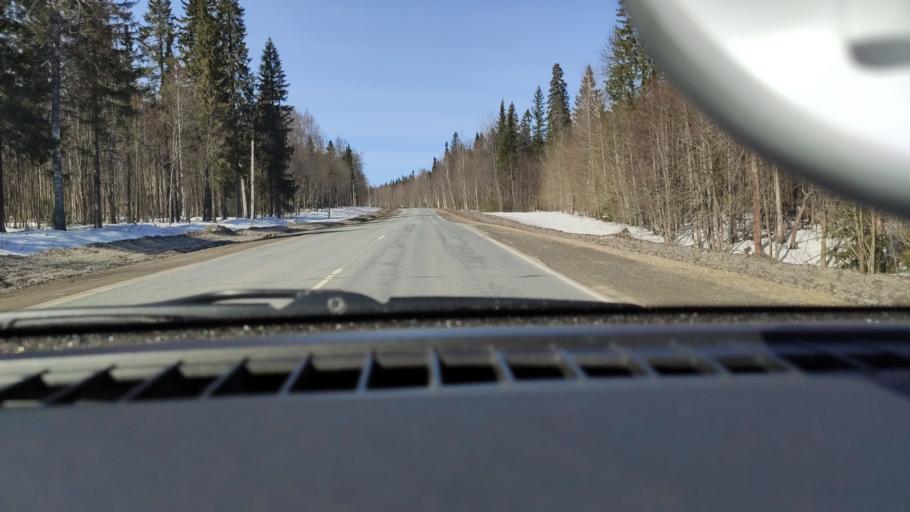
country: RU
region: Perm
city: Perm
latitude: 58.2048
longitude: 56.1997
